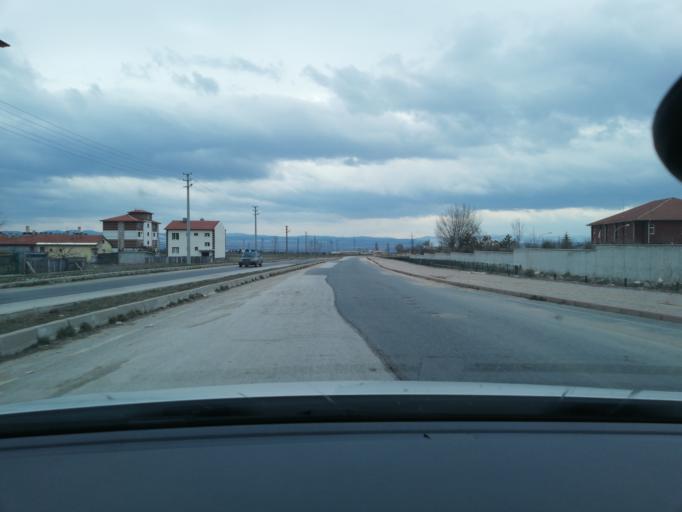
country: TR
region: Bolu
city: Gerede
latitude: 40.7872
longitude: 32.2039
